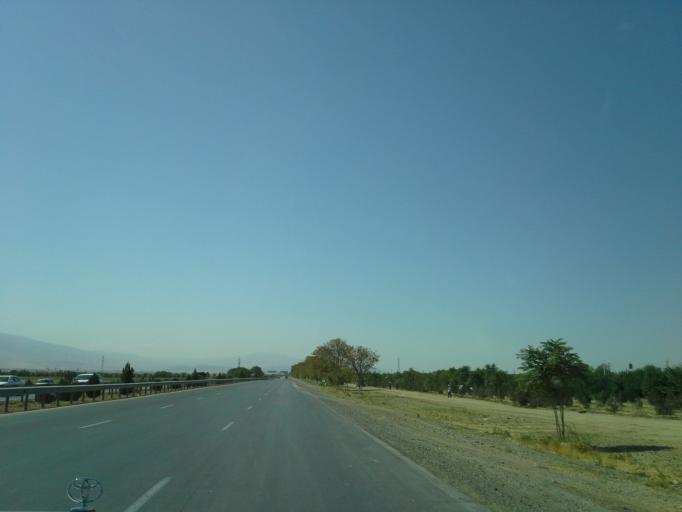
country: TM
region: Ahal
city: Annau
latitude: 37.9026
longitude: 58.5611
